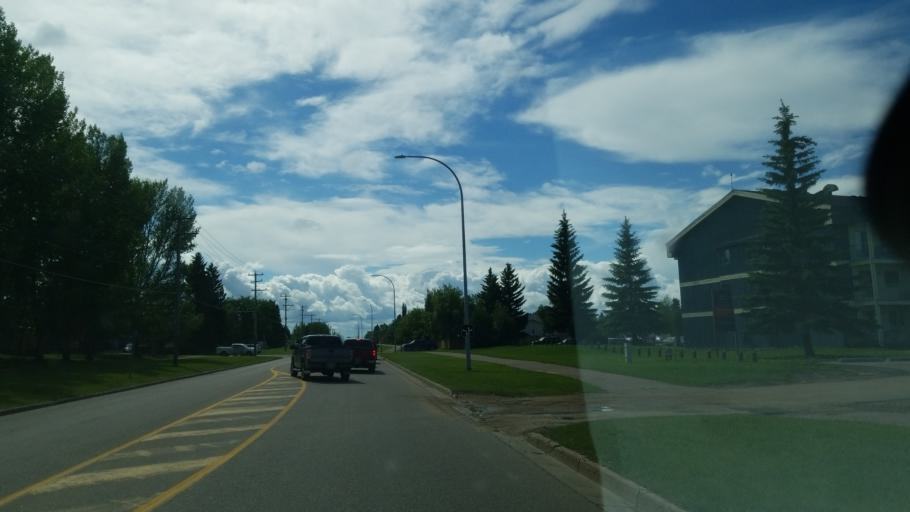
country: CA
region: Saskatchewan
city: Lloydminster
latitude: 53.2708
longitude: -110.0102
